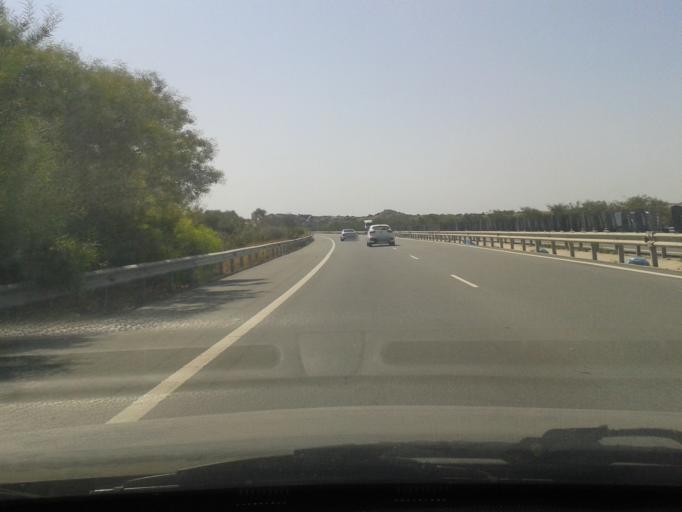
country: CY
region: Larnaka
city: Kofinou
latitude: 34.7762
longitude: 33.3404
